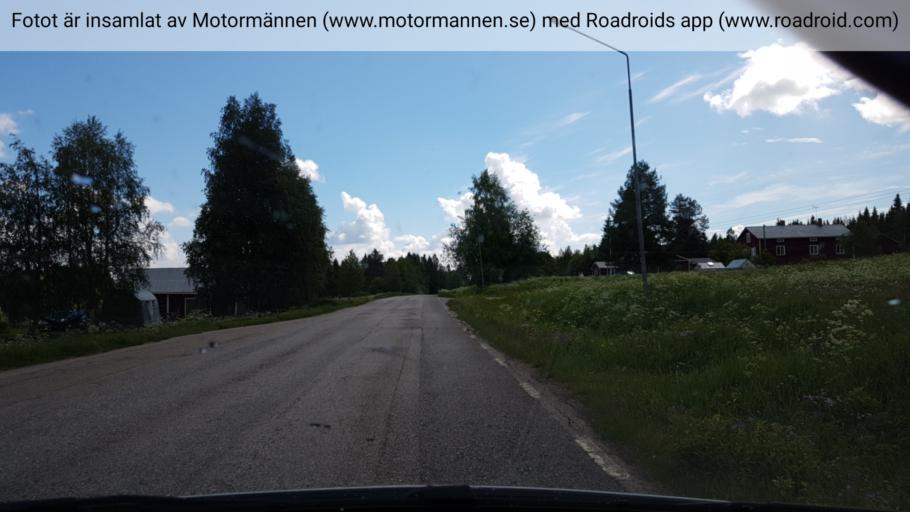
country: FI
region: Lapland
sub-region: Torniolaakso
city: Ylitornio
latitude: 66.1738
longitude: 23.8108
